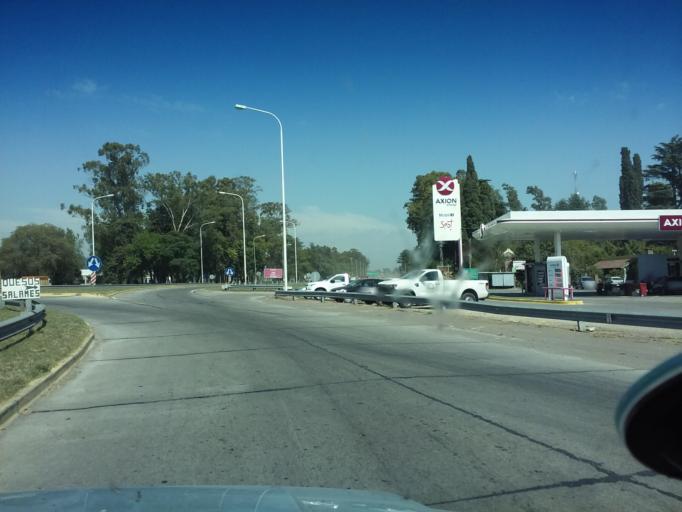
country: AR
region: Buenos Aires
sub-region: Partido de Nueve de Julio
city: Nueve de Julio
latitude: -35.4680
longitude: -60.8499
